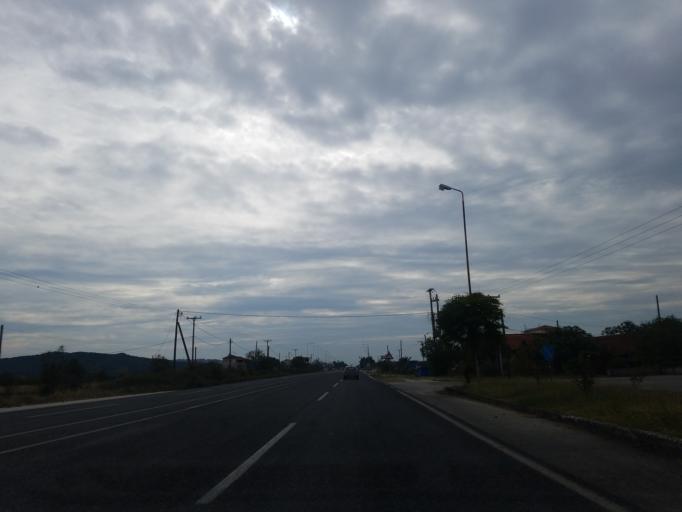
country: GR
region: Thessaly
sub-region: Trikala
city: Kalampaka
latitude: 39.6756
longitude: 21.6602
